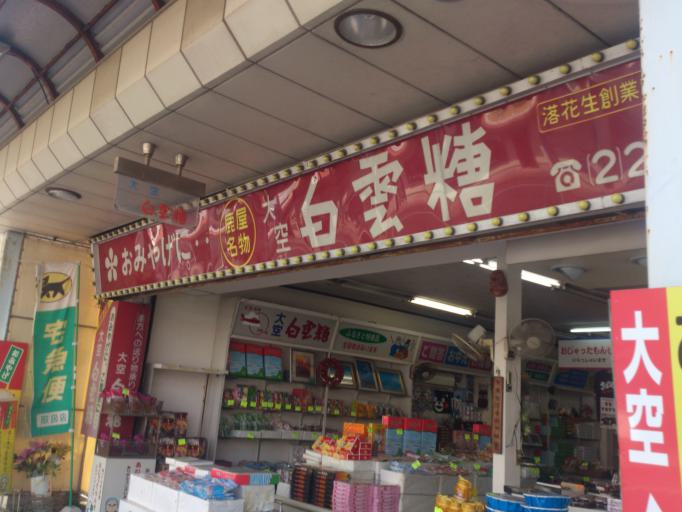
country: JP
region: Kagoshima
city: Kanoya
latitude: 31.3847
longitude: 130.8515
